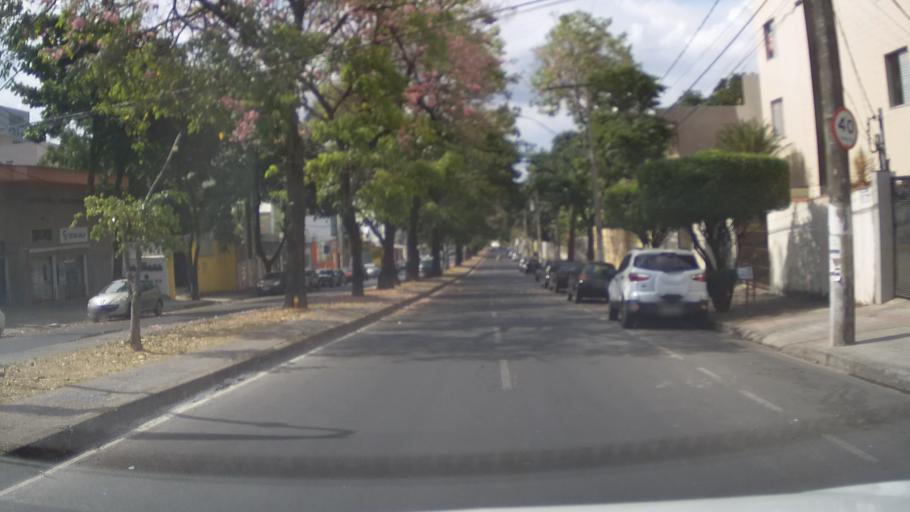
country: BR
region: Minas Gerais
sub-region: Belo Horizonte
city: Belo Horizonte
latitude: -19.8429
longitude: -43.9739
